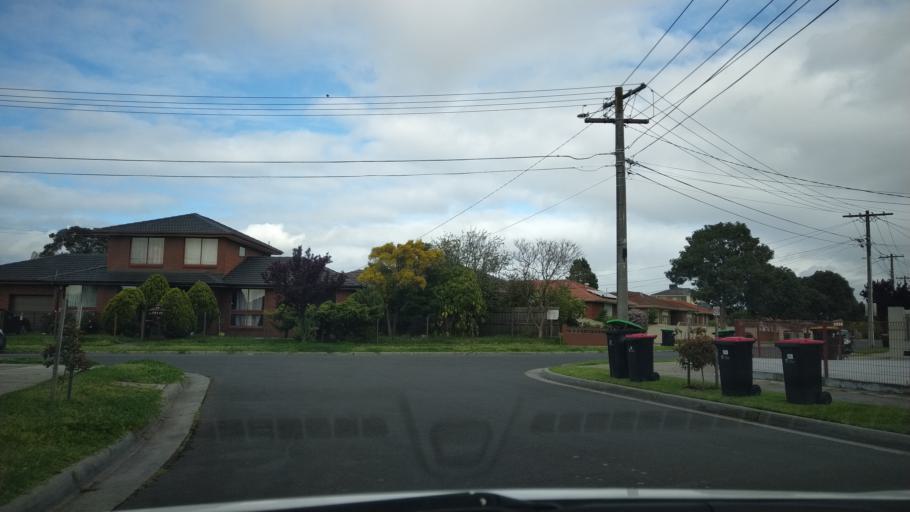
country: AU
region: Victoria
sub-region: Greater Dandenong
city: Keysborough
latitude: -37.9907
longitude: 145.1816
